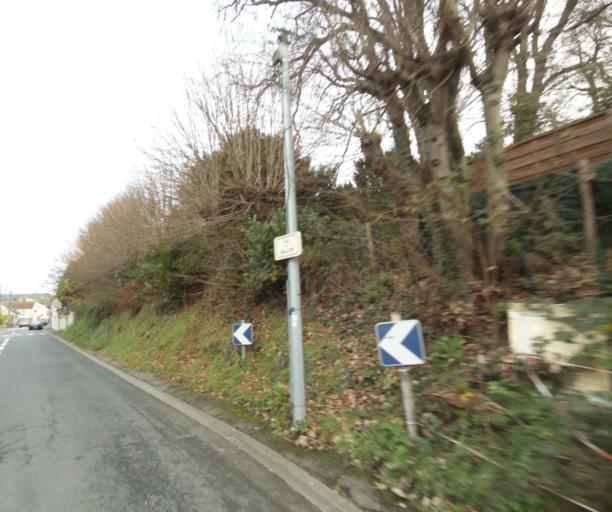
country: FR
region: Pays de la Loire
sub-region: Departement de la Sarthe
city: Coulaines
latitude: 48.0172
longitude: 0.2041
